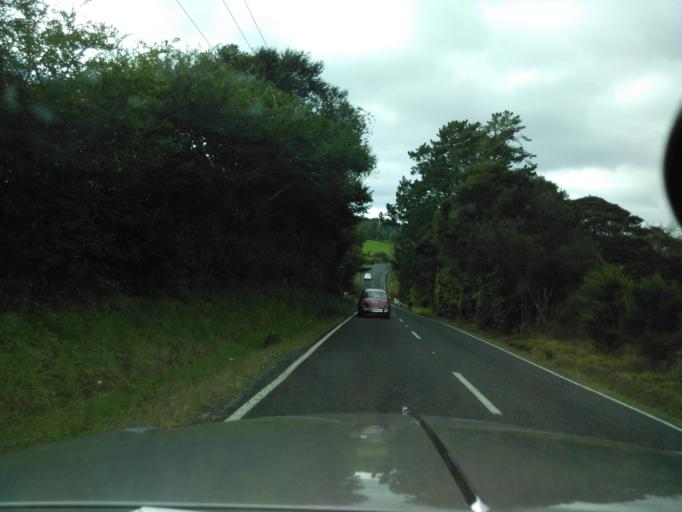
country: NZ
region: Auckland
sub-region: Auckland
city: Red Hill
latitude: -37.1138
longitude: 175.0732
